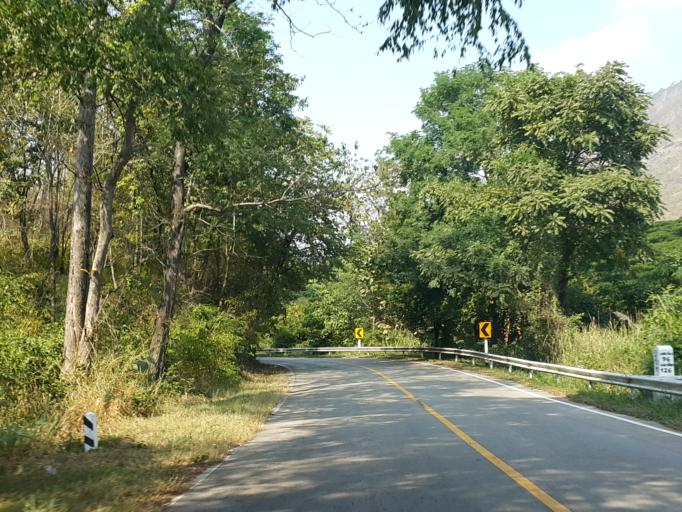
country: TH
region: Chiang Mai
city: Hot
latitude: 18.2243
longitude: 98.5709
